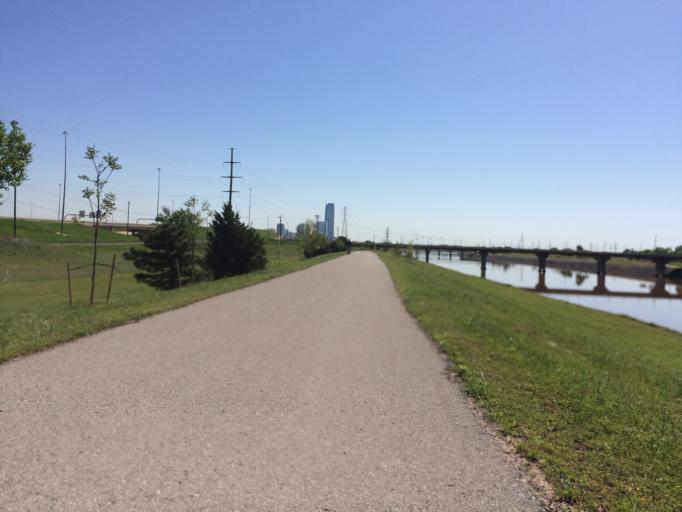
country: US
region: Oklahoma
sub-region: Oklahoma County
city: Oklahoma City
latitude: 35.4596
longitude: -97.5586
